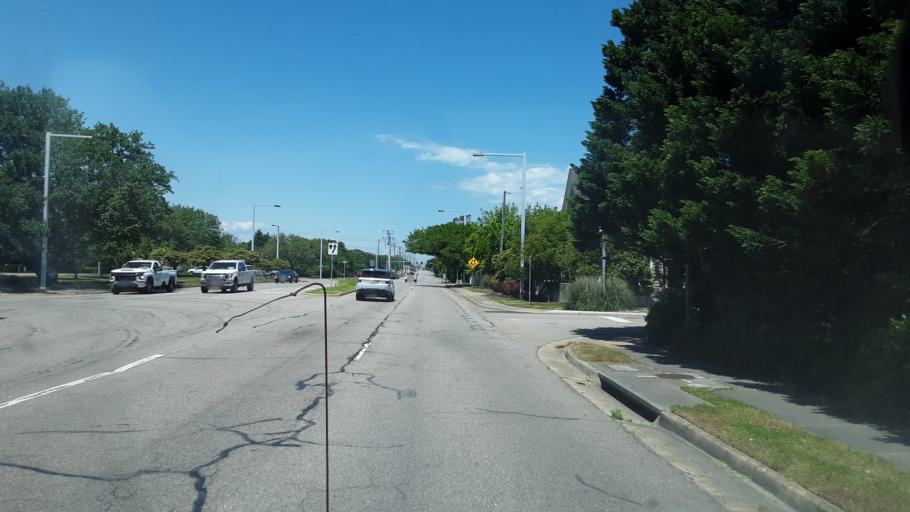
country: US
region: Virginia
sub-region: City of Virginia Beach
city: Virginia Beach
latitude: 36.8718
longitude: -75.9826
